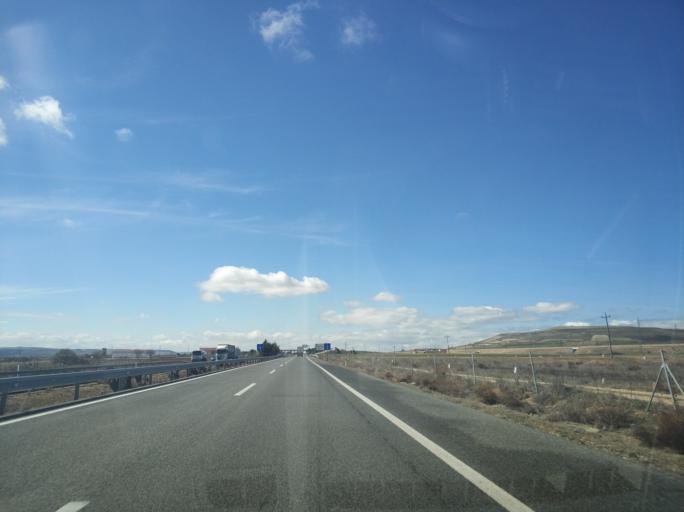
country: ES
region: Castille and Leon
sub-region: Provincia de Burgos
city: Villazopeque
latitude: 42.2083
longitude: -4.0123
